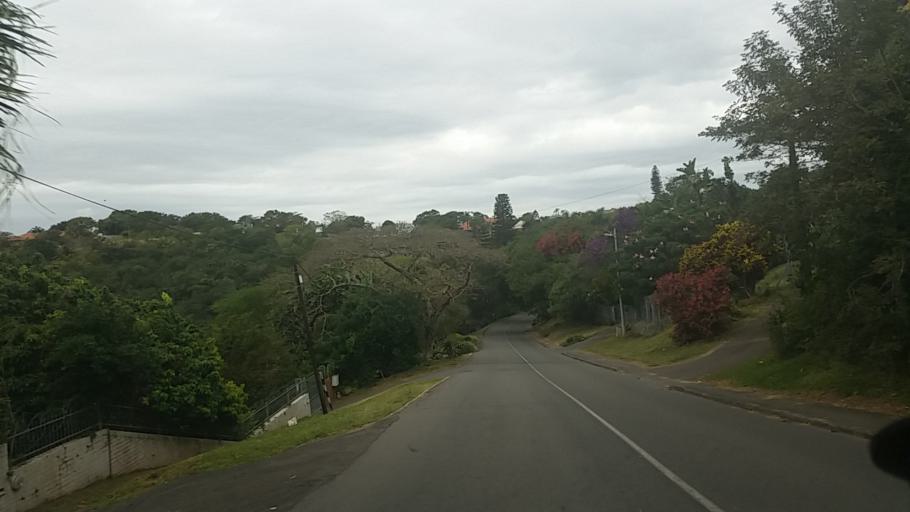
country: ZA
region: KwaZulu-Natal
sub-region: eThekwini Metropolitan Municipality
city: Berea
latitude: -29.8407
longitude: 30.9282
